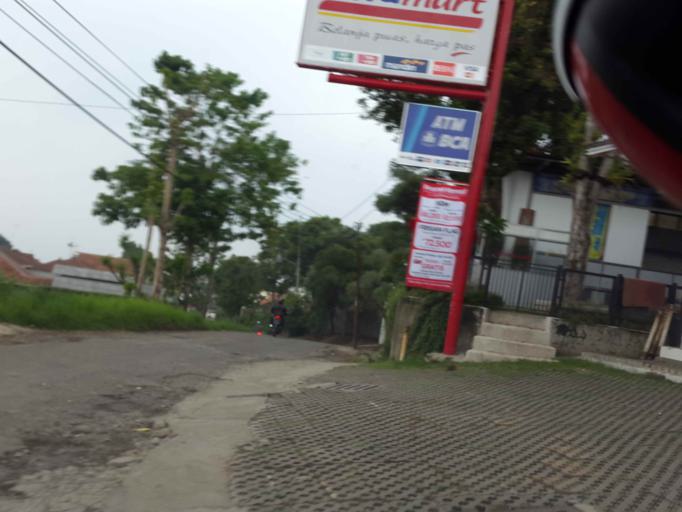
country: ID
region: West Java
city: Lembang
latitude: -6.8408
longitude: 107.5851
